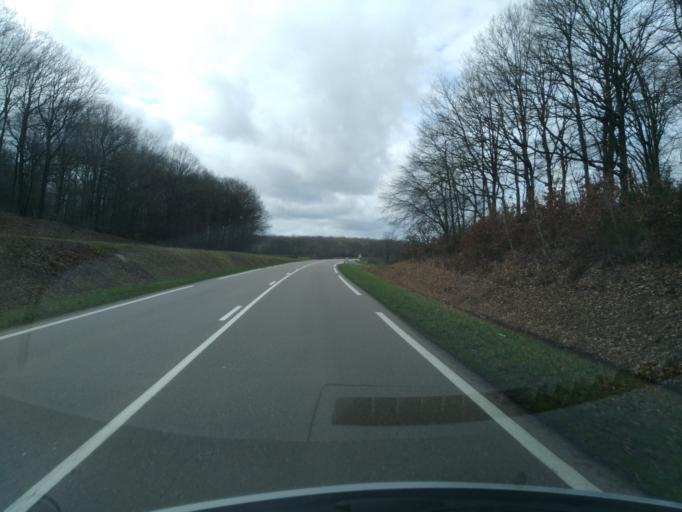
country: FR
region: Bourgogne
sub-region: Departement de Saone-et-Loire
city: Torcy
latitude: 46.7674
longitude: 4.4373
